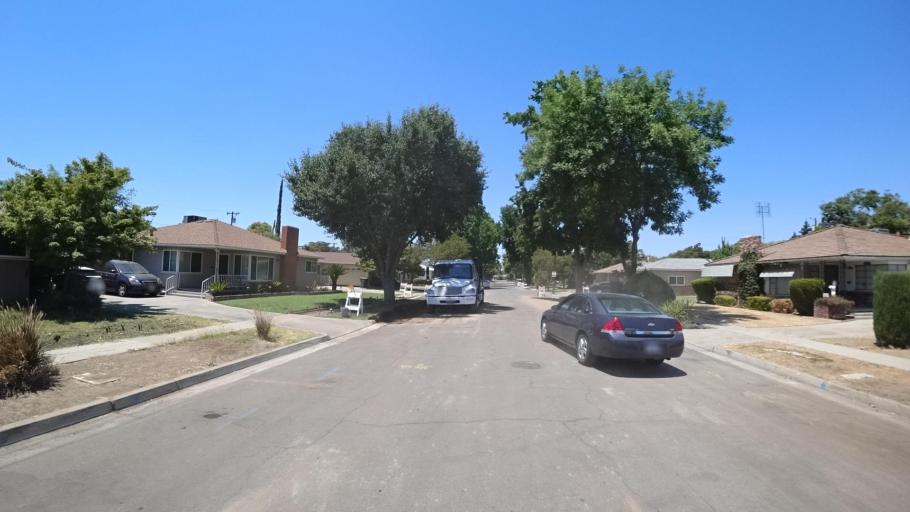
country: US
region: California
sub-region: Fresno County
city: Fresno
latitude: 36.7966
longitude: -119.7680
